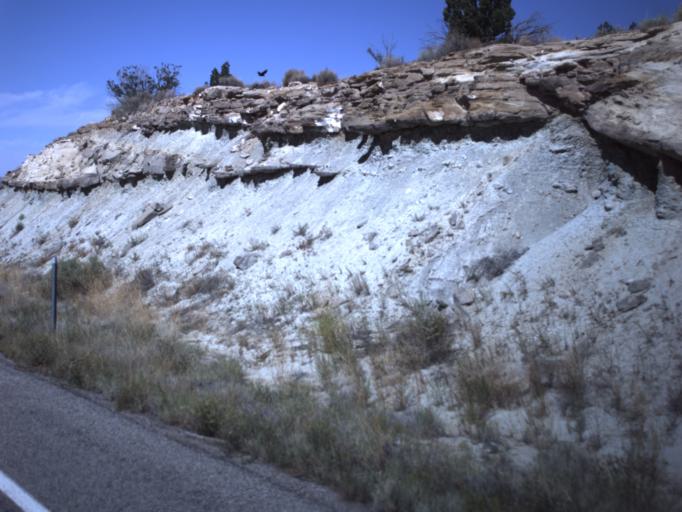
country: US
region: Colorado
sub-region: Montezuma County
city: Towaoc
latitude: 37.1912
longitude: -109.1352
